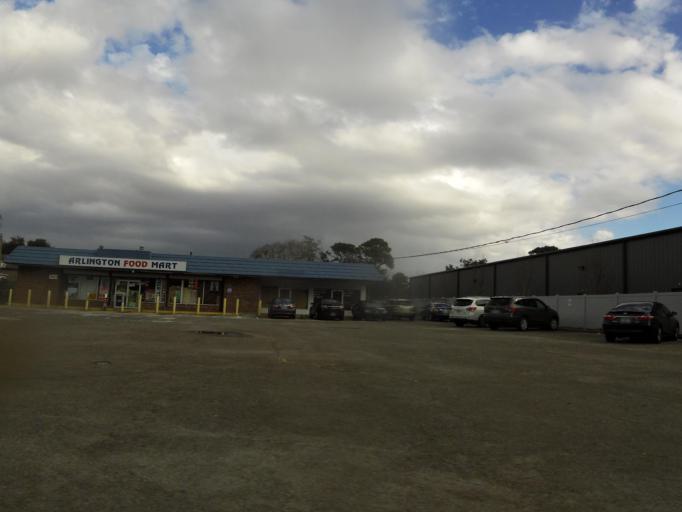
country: US
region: Florida
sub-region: Duval County
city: Jacksonville
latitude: 30.3656
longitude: -81.5879
